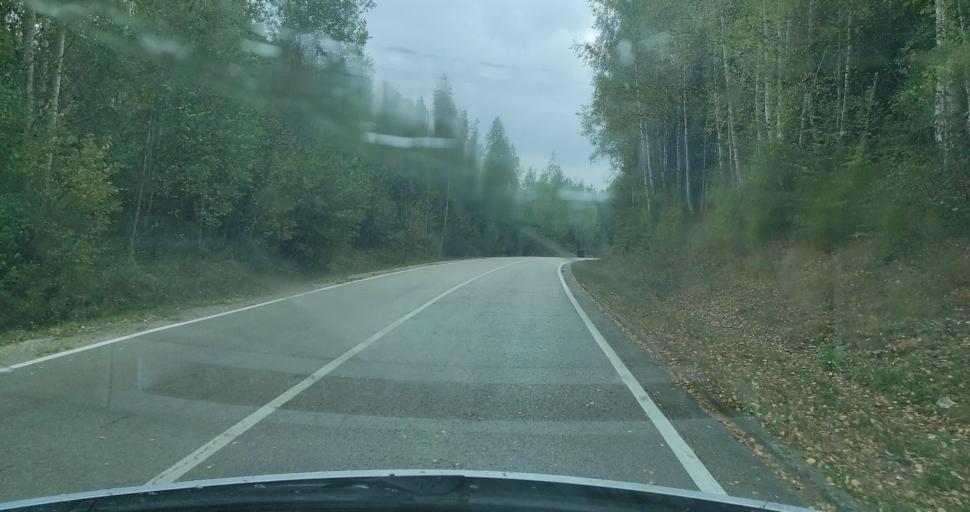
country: RS
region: Central Serbia
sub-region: Jablanicki Okrug
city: Crna Trava
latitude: 42.7289
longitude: 22.3357
